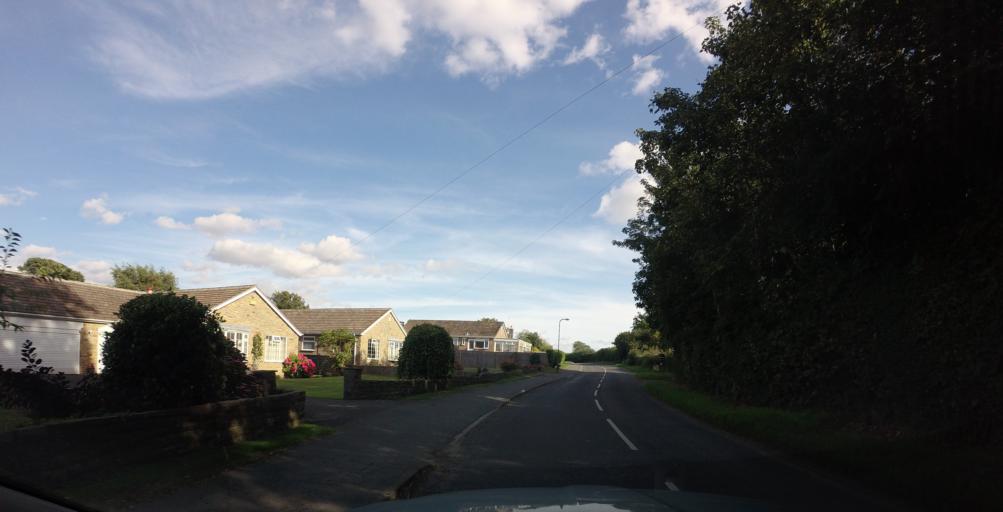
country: GB
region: England
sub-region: North Yorkshire
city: Ripon
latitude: 54.0904
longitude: -1.5018
